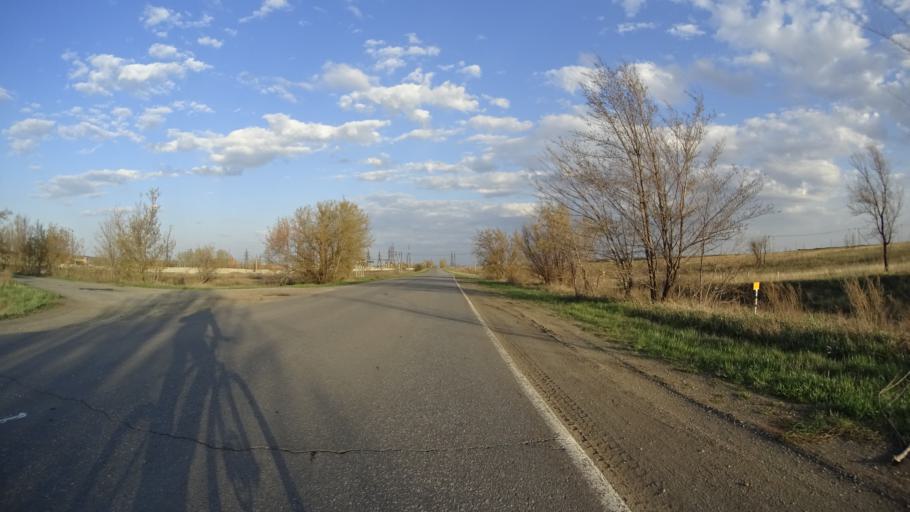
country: RU
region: Chelyabinsk
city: Troitsk
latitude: 54.0604
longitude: 61.5782
